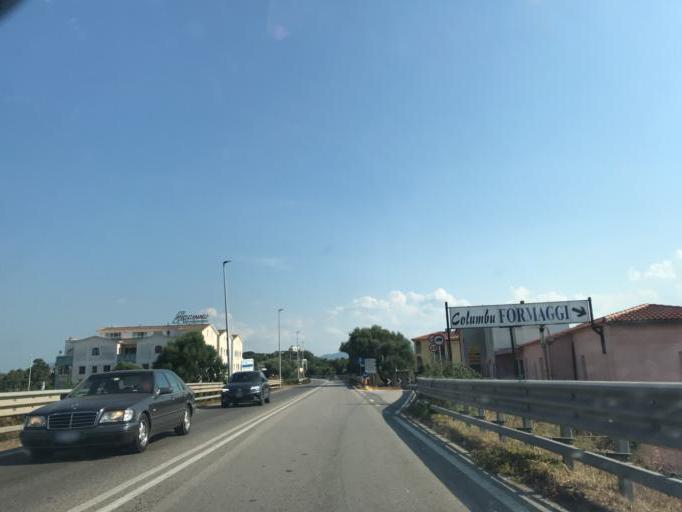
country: IT
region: Sardinia
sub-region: Provincia di Olbia-Tempio
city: Olbia
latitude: 40.9157
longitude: 9.5016
